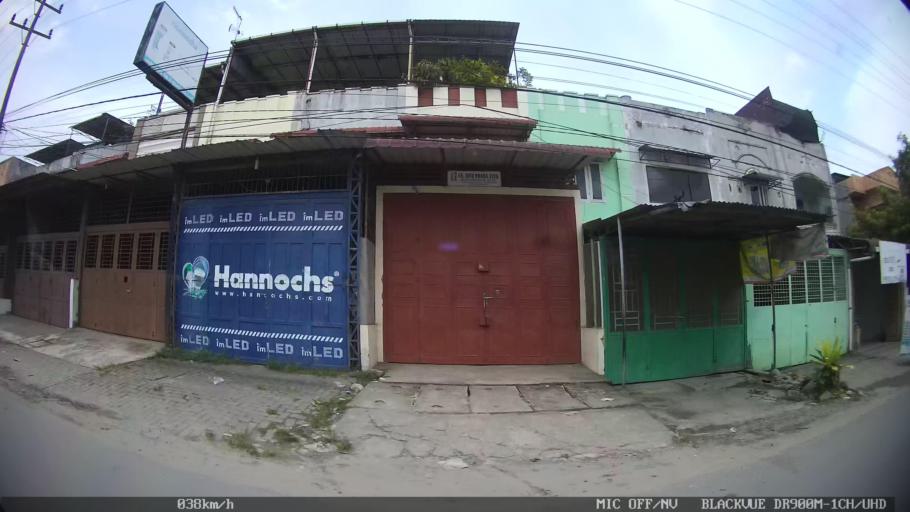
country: ID
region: North Sumatra
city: Labuhan Deli
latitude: 3.7100
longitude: 98.6643
